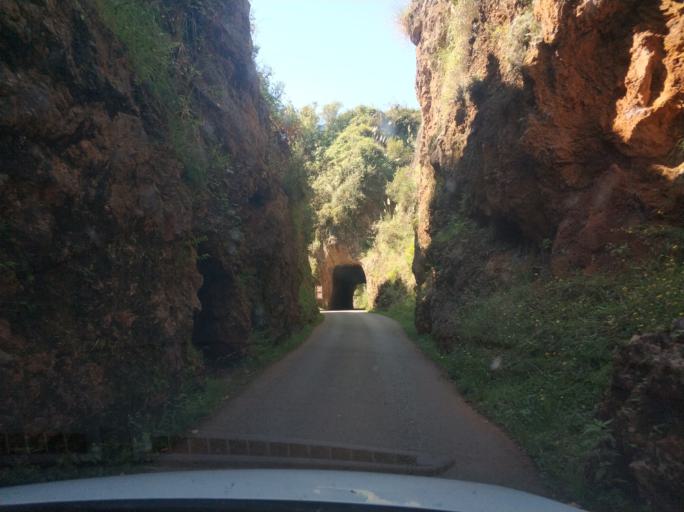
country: ES
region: Cantabria
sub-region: Provincia de Cantabria
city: Penagos
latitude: 43.3633
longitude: -3.8303
